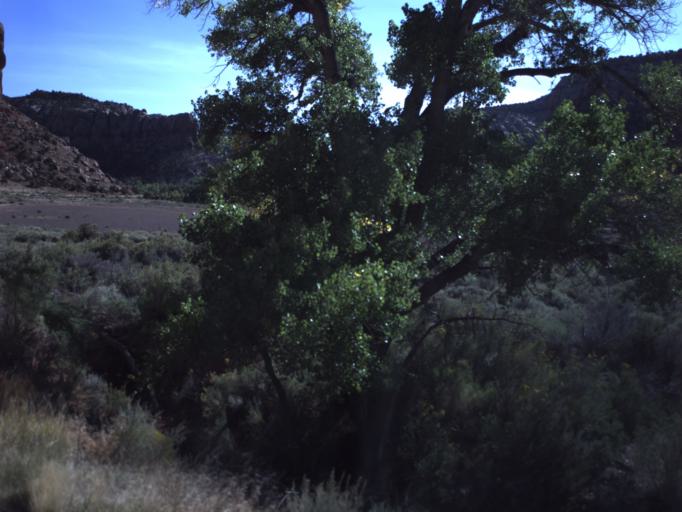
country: US
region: Utah
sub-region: San Juan County
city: Monticello
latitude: 38.0469
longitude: -109.5527
